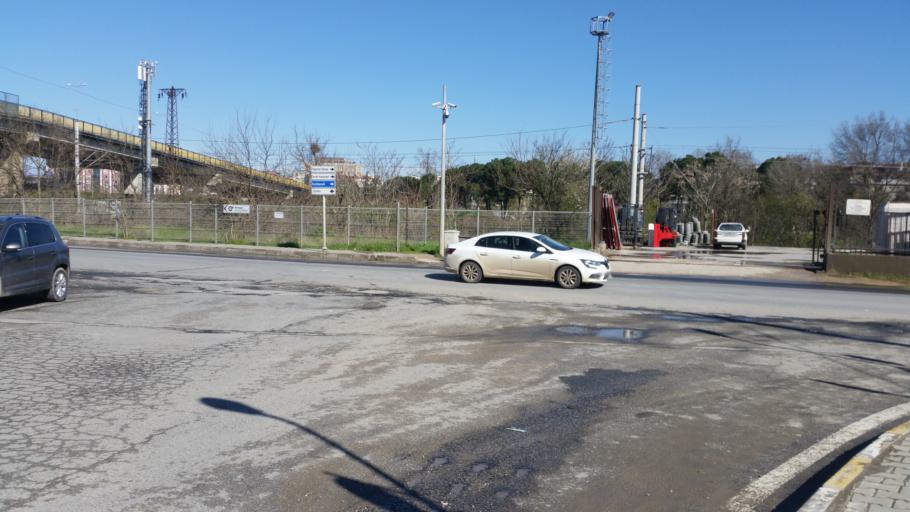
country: TR
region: Tekirdag
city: Cerkezkoey
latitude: 41.2792
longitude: 28.0025
